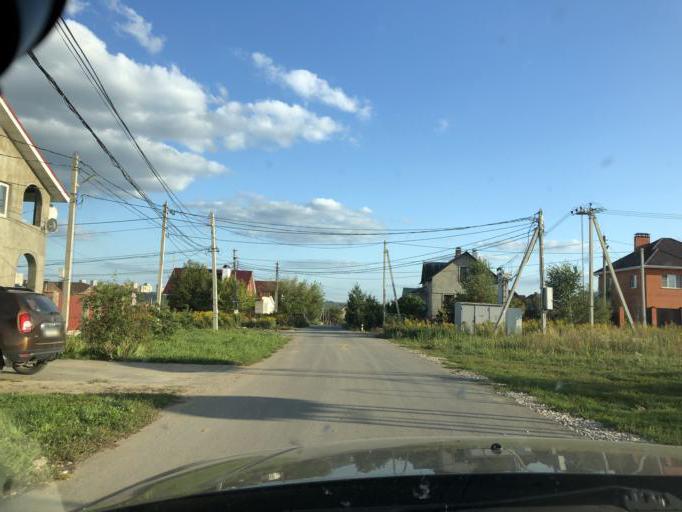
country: RU
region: Tula
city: Kosaya Gora
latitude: 54.1763
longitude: 37.5442
